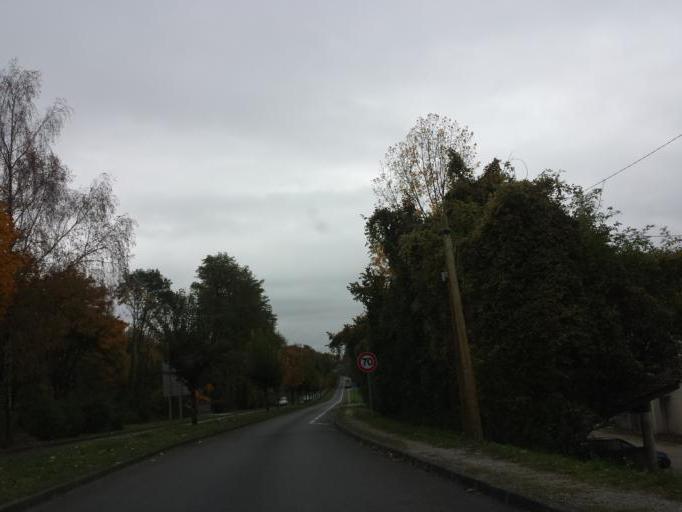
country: FR
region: Poitou-Charentes
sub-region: Departement de la Charente
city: La Couronne
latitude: 45.6283
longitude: 0.1174
